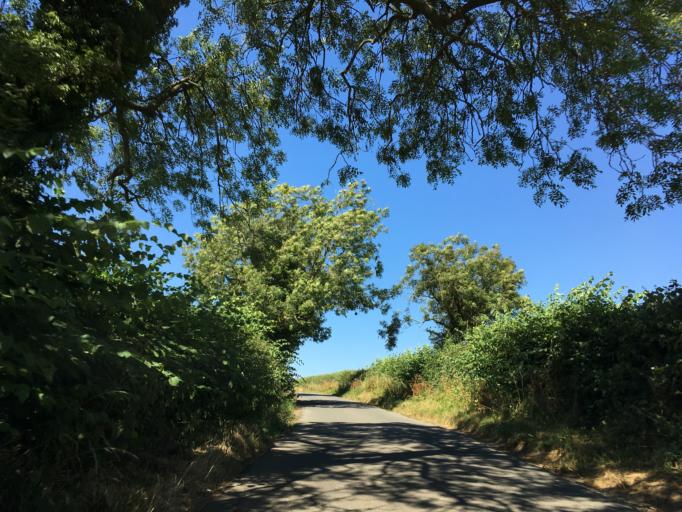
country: GB
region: England
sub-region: South Gloucestershire
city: Chipping Sodbury
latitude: 51.5155
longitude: -2.3938
